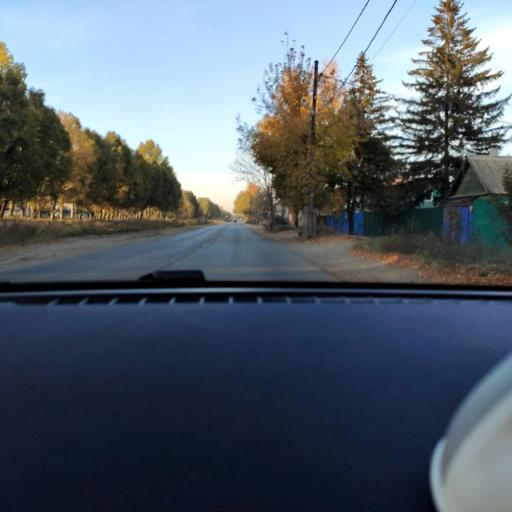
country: RU
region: Samara
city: Smyshlyayevka
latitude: 53.2339
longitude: 50.3078
